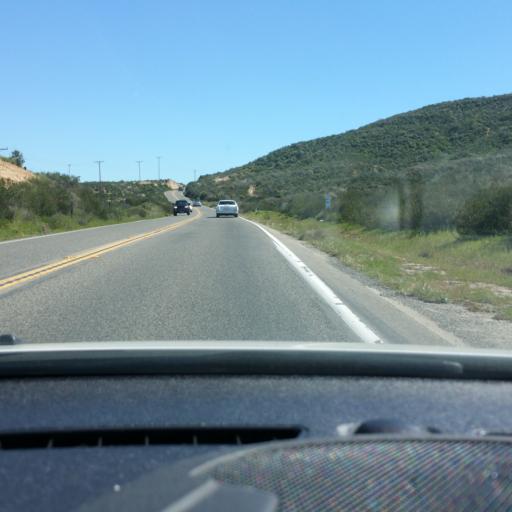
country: US
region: California
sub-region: Riverside County
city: Aguanga
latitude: 33.4679
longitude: -116.9934
